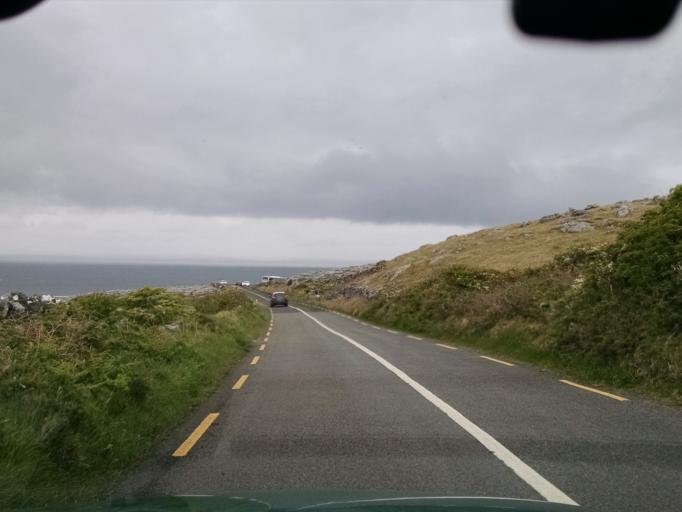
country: IE
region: Connaught
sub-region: County Galway
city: Bearna
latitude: 53.1387
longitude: -9.2756
